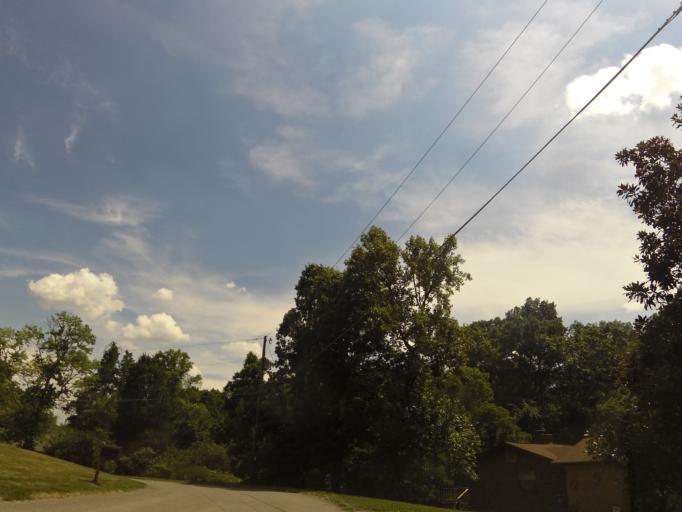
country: US
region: Tennessee
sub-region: Knox County
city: Knoxville
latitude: 35.9195
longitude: -83.8307
